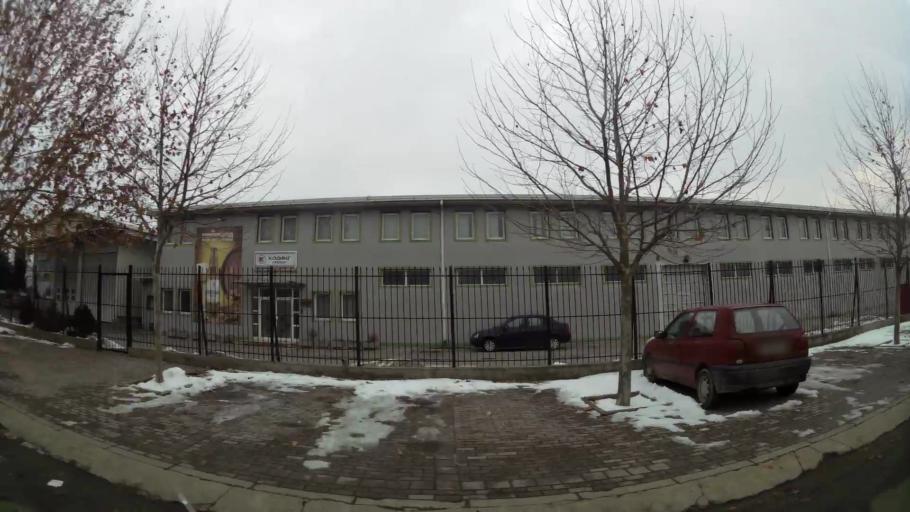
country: MK
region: Saraj
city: Saraj
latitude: 42.0186
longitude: 21.3616
